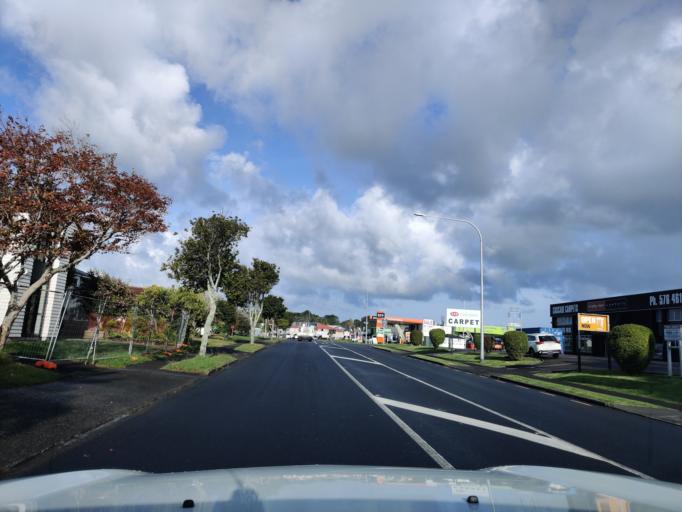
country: NZ
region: Auckland
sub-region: Auckland
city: Pakuranga
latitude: -36.9125
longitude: 174.9016
